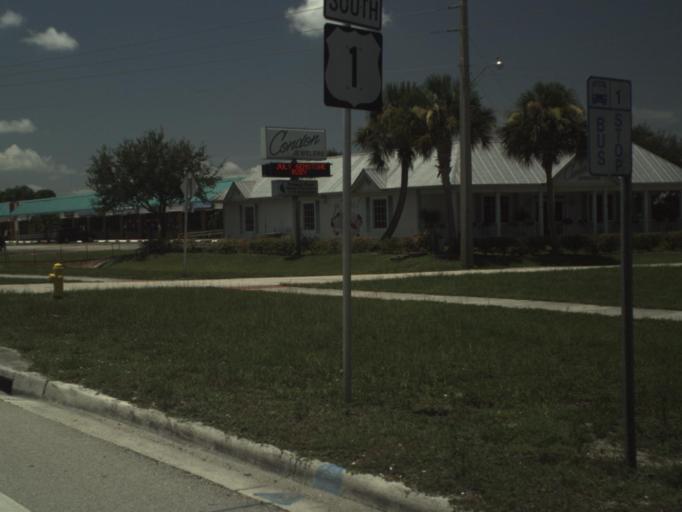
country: US
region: Florida
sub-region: Martin County
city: North River Shores
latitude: 27.2222
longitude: -80.2636
